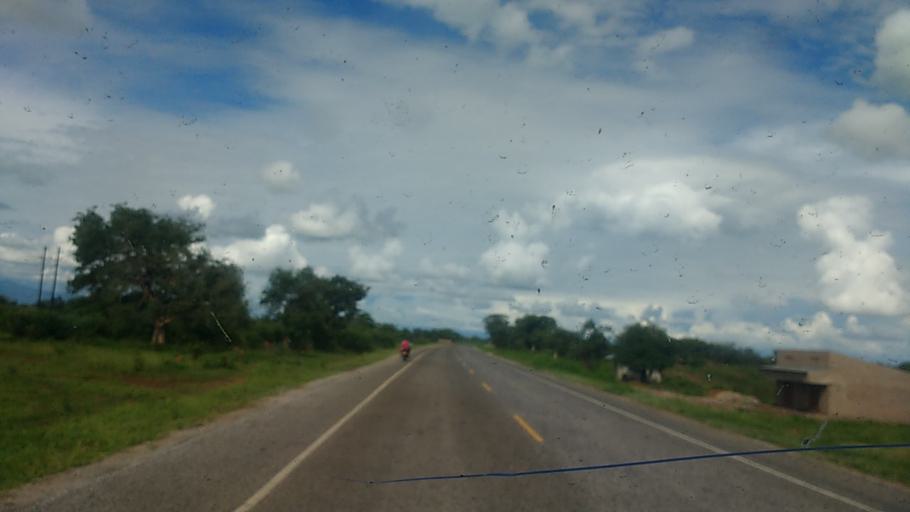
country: UG
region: Eastern Region
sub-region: Katakwi District
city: Katakwi
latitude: 1.9199
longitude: 33.9984
